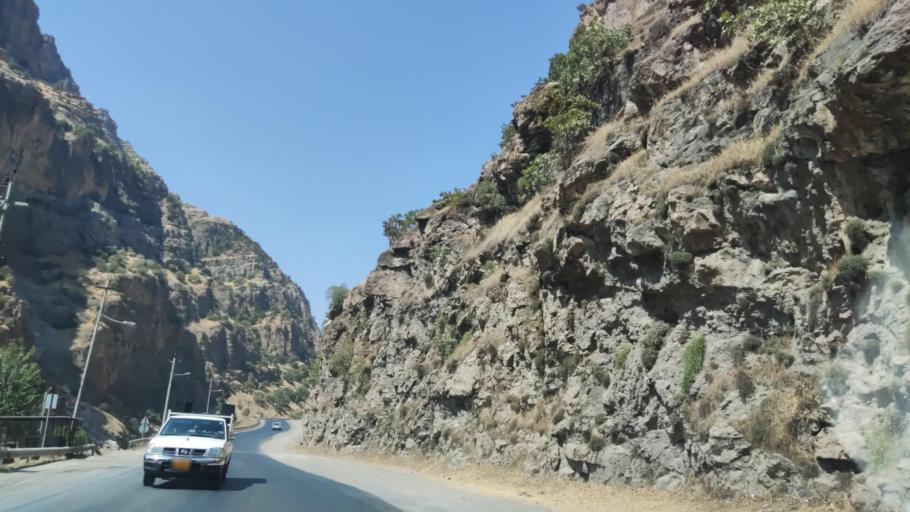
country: IQ
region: Arbil
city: Ruwandiz
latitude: 36.6316
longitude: 44.4873
